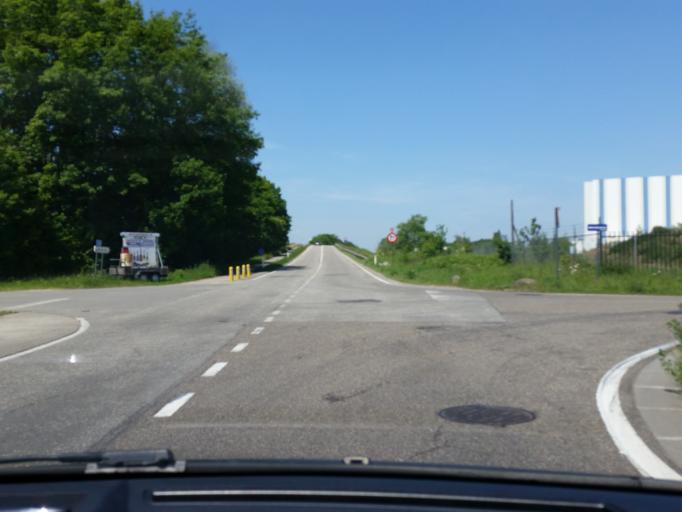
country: BE
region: Flanders
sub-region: Provincie Antwerpen
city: Mechelen
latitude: 51.0111
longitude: 4.4542
